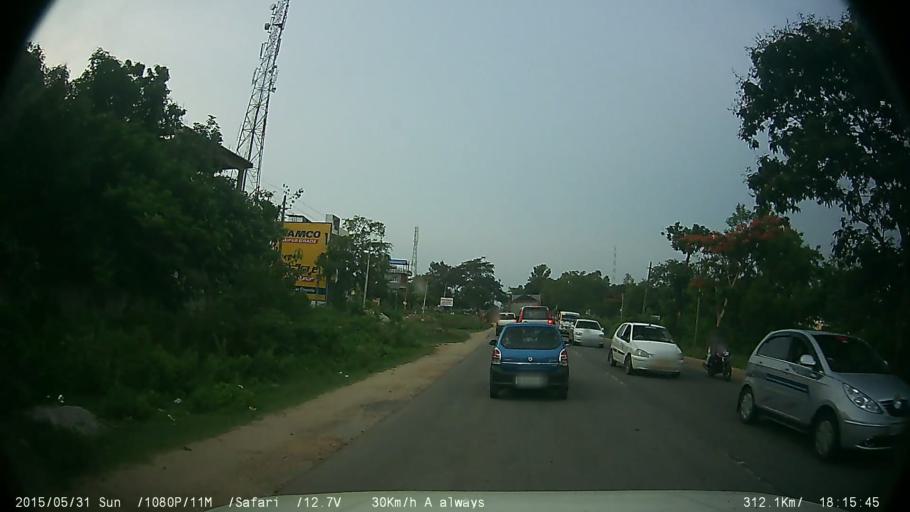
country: IN
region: Karnataka
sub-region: Mysore
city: Nanjangud
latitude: 12.1125
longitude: 76.6736
